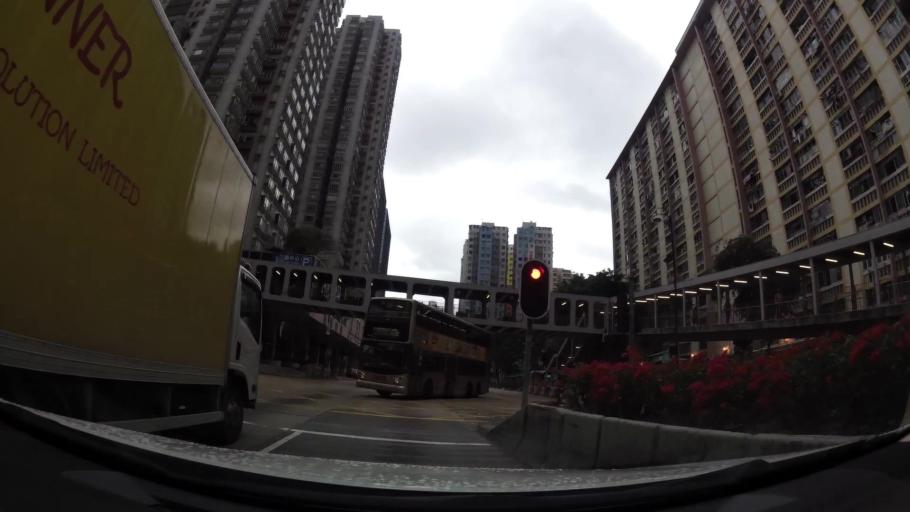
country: HK
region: Tsuen Wan
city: Tsuen Wan
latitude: 22.3745
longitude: 114.1142
